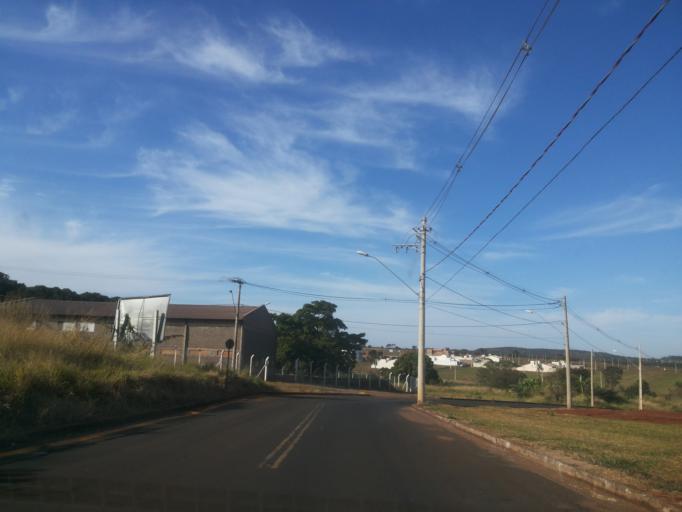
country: BR
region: Minas Gerais
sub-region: Ituiutaba
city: Ituiutaba
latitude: -18.9958
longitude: -49.4665
